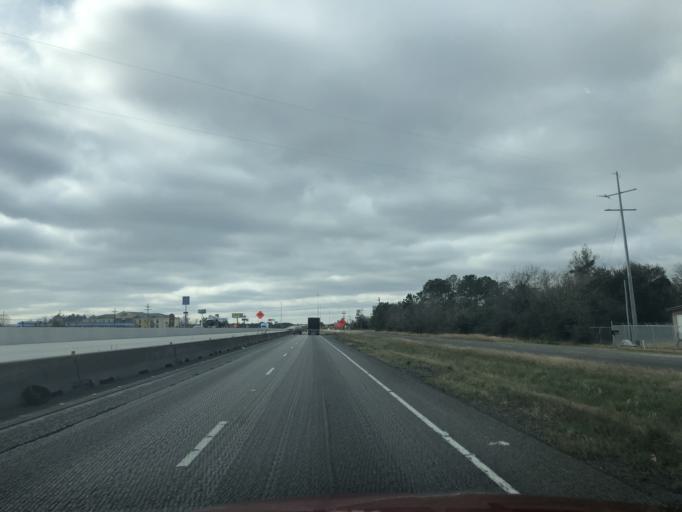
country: US
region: Texas
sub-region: Chambers County
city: Winnie
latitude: 29.8400
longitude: -94.3783
